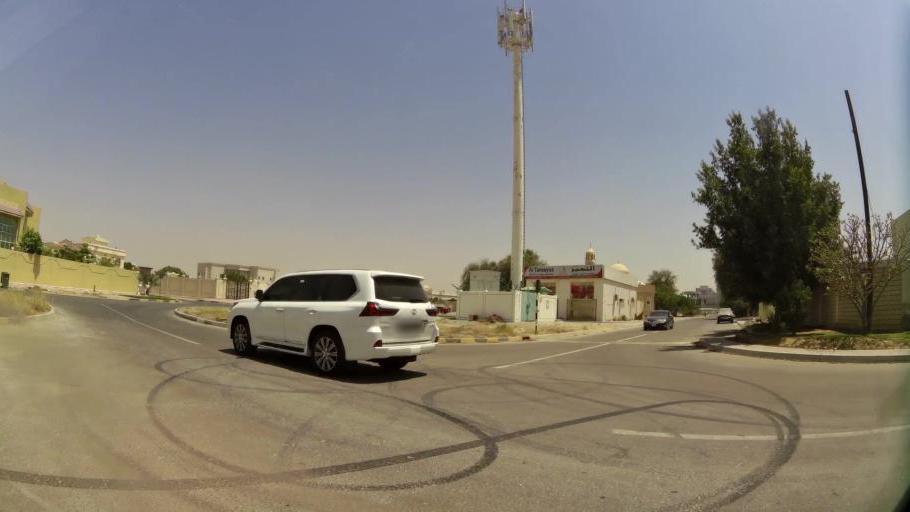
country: AE
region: Ajman
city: Ajman
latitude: 25.4193
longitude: 55.5058
